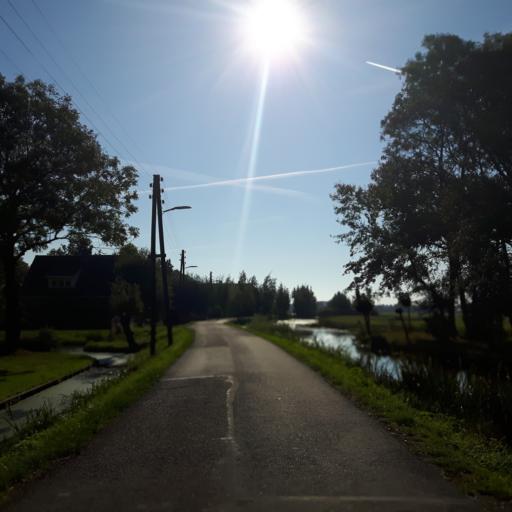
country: NL
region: South Holland
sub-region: Gemeente Schoonhoven
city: Schoonhoven
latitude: 51.9640
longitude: 4.8428
